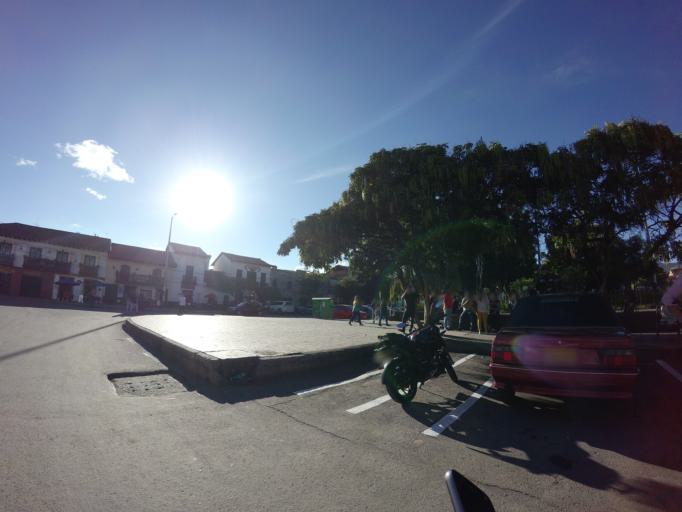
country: CO
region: Cundinamarca
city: Ubate
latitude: 5.3063
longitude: -73.8147
